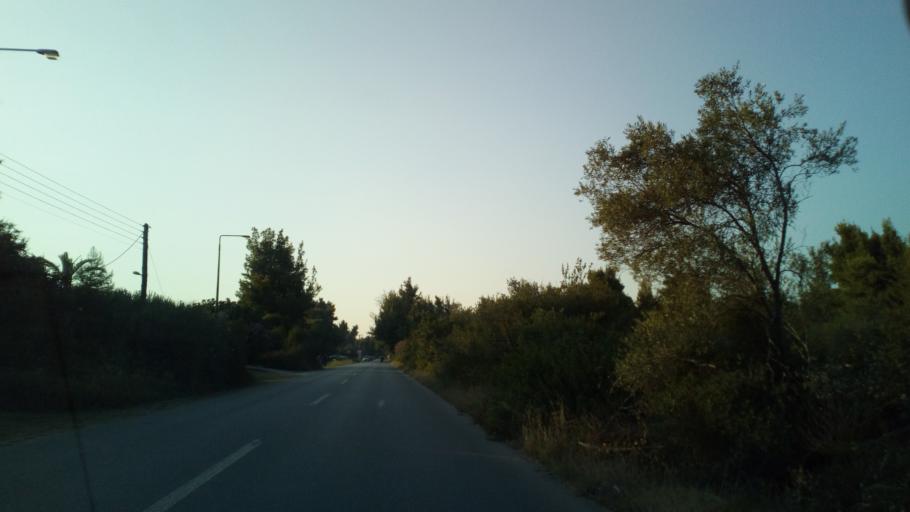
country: GR
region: Central Macedonia
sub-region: Nomos Chalkidikis
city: Pefkochori
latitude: 39.9692
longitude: 23.6709
